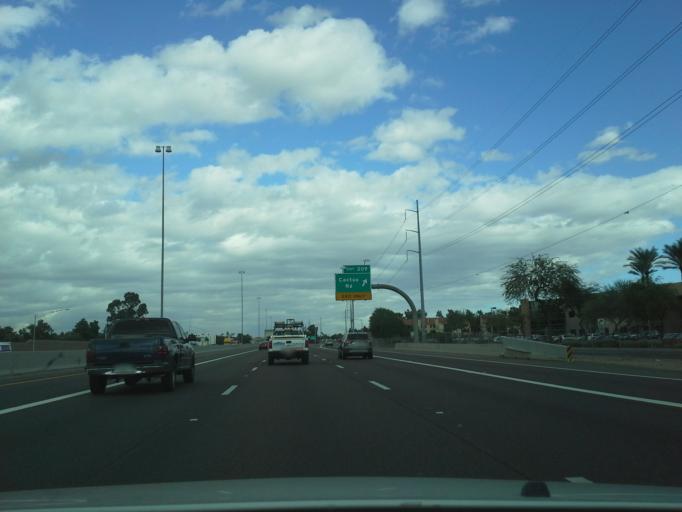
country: US
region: Arizona
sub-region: Maricopa County
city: Glendale
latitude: 33.5900
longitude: -112.1168
